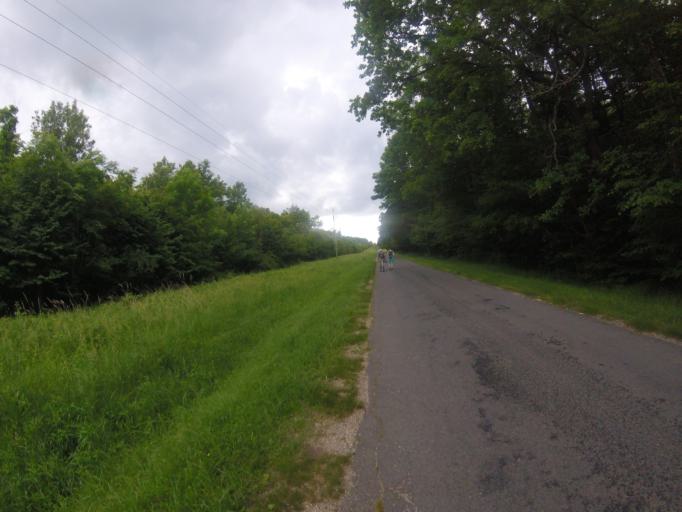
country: HU
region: Veszprem
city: Urkut
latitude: 47.0571
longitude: 17.6668
